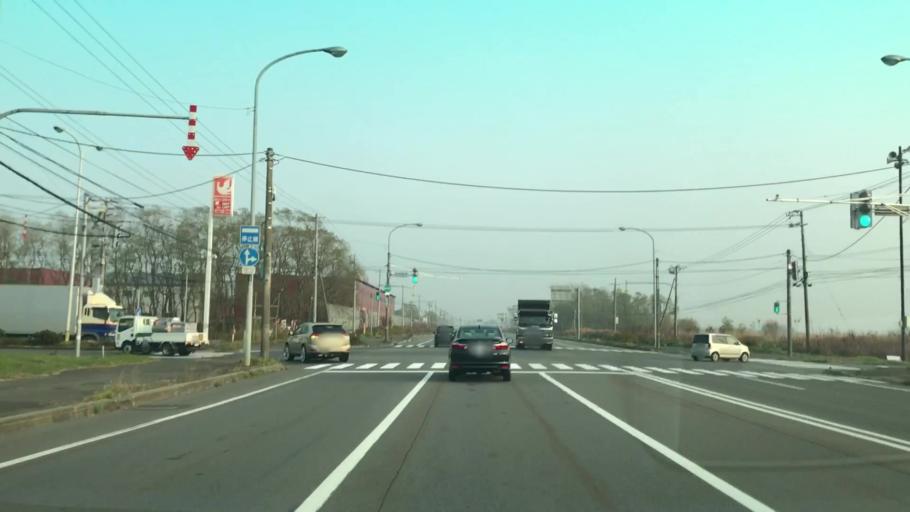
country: JP
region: Hokkaido
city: Ishikari
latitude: 43.2080
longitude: 141.3330
